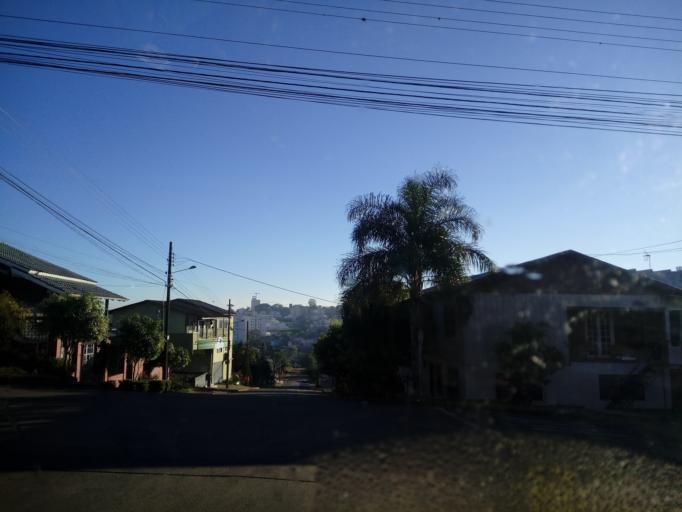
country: BR
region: Santa Catarina
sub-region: Chapeco
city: Chapeco
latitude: -27.1188
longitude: -52.6210
